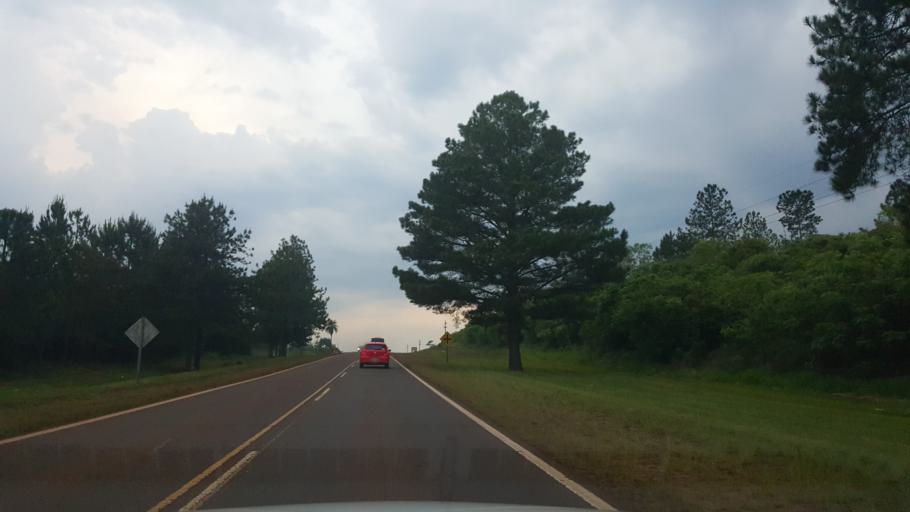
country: AR
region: Misiones
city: Gobernador Roca
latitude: -27.1679
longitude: -55.4434
